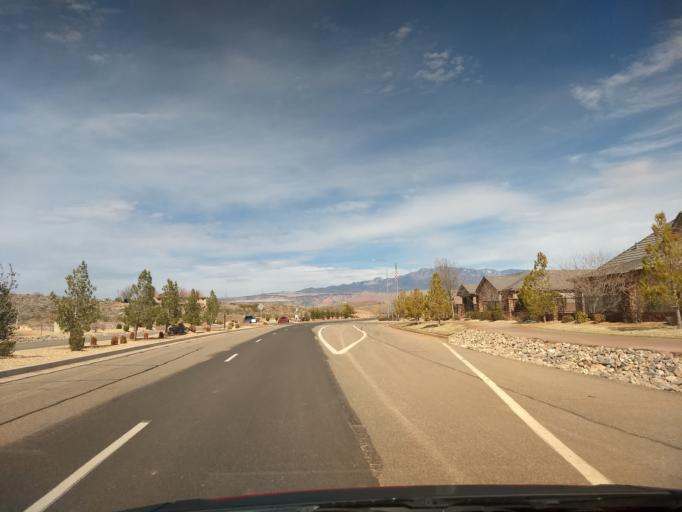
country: US
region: Utah
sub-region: Washington County
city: Washington
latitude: 37.0697
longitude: -113.4939
